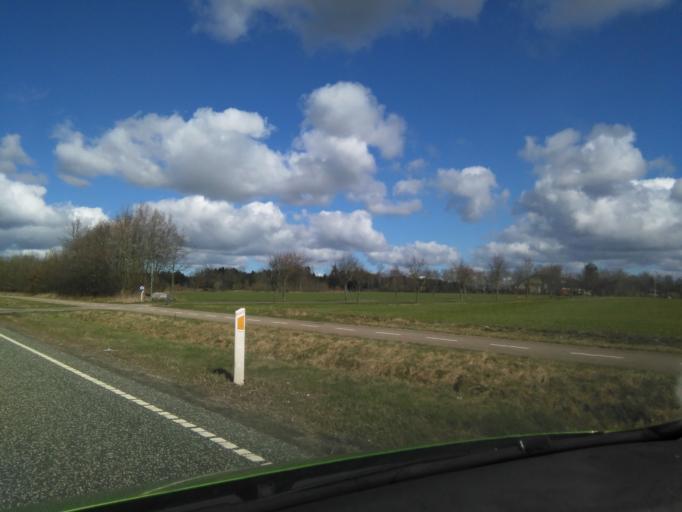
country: DK
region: Central Jutland
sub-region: Ikast-Brande Kommune
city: Bording Kirkeby
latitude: 56.1409
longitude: 9.3514
